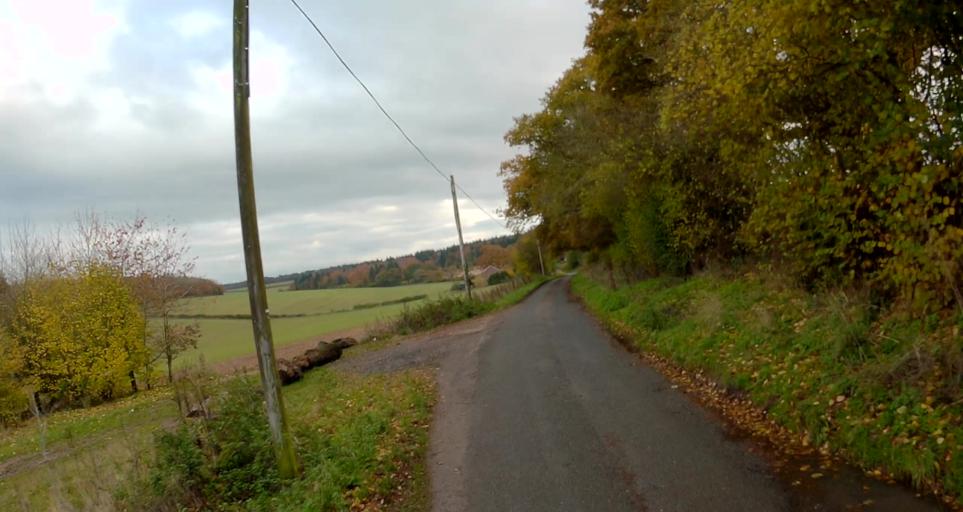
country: GB
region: England
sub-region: Hampshire
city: Long Sutton
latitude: 51.2126
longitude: -0.9582
